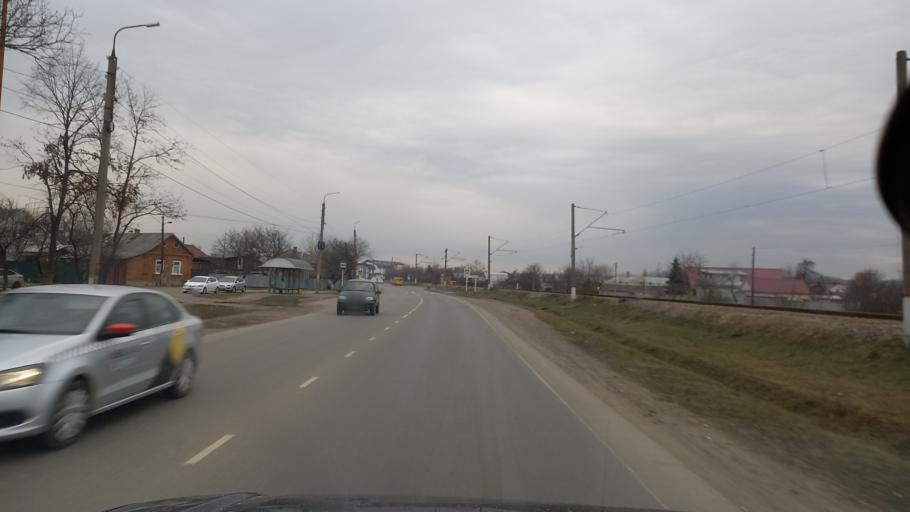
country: RU
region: Adygeya
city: Maykop
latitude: 44.5907
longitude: 40.1312
